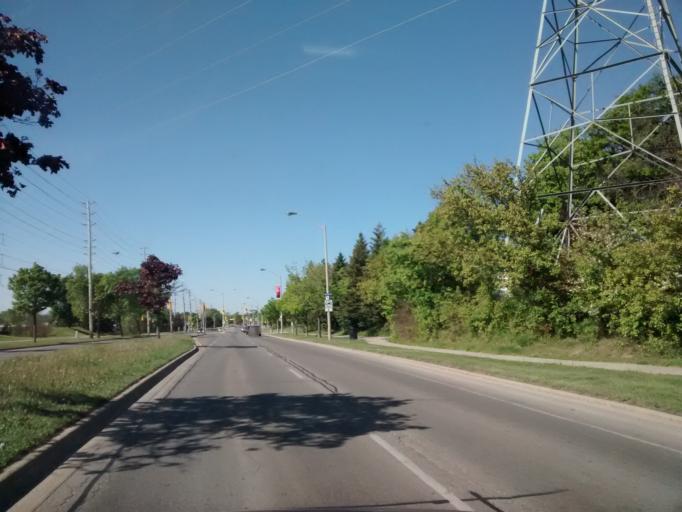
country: CA
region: Ontario
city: Burlington
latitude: 43.3680
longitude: -79.8182
